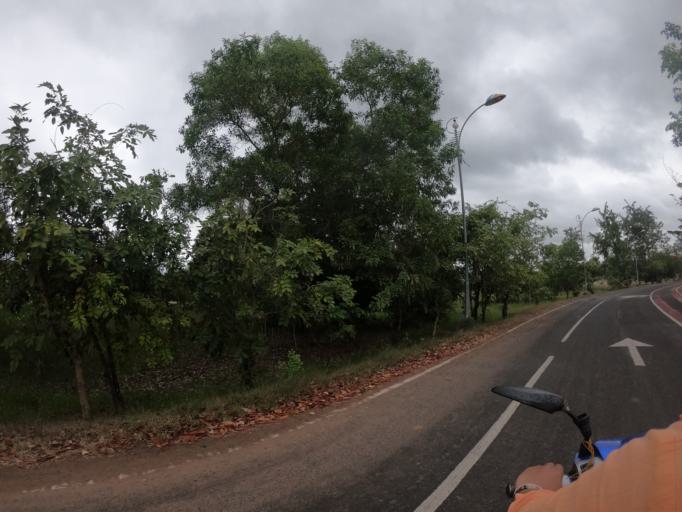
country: TH
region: Roi Et
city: Selaphum
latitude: 16.1436
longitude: 103.8807
